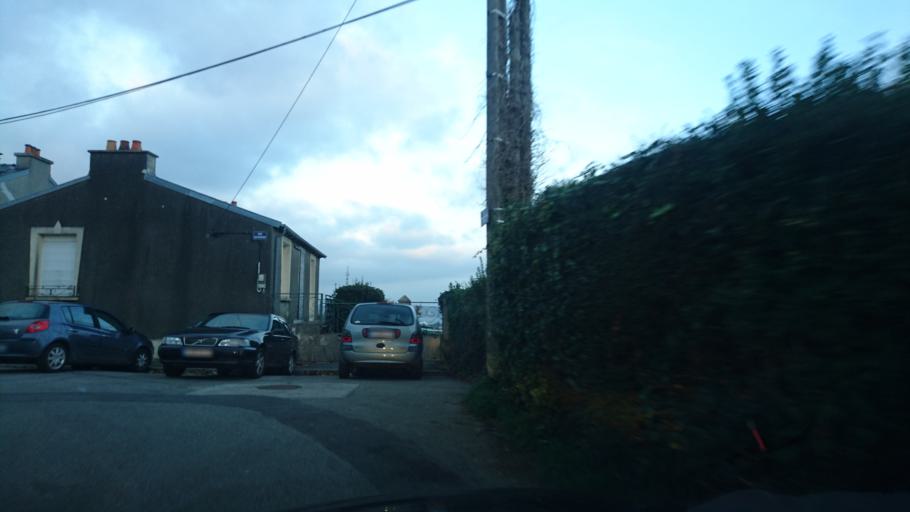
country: FR
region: Brittany
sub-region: Departement du Finistere
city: Brest
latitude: 48.3895
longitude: -4.4645
